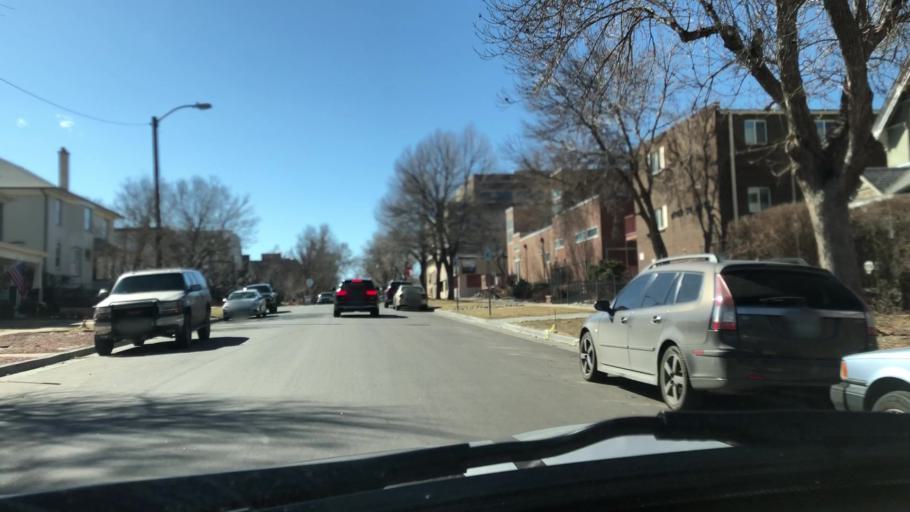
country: US
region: Colorado
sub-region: Denver County
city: Denver
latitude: 39.7490
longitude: -104.9647
